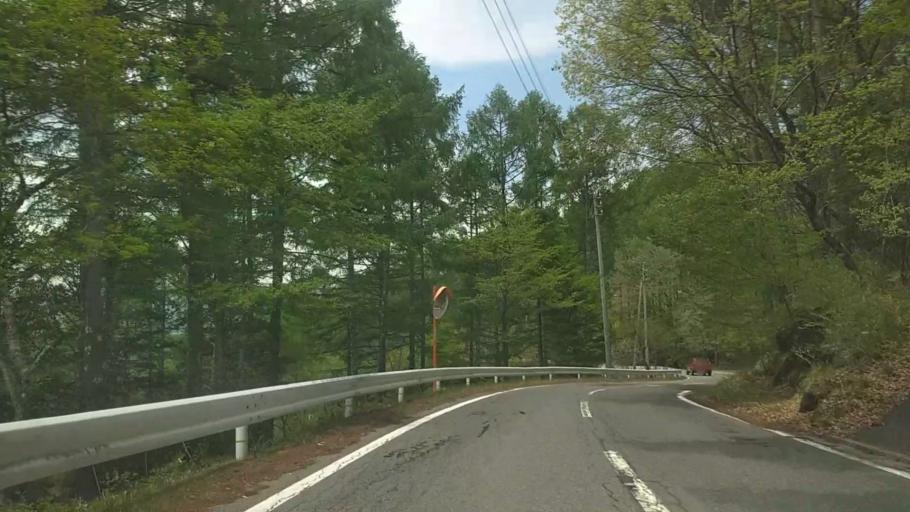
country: JP
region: Nagano
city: Chino
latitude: 36.0423
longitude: 138.2770
